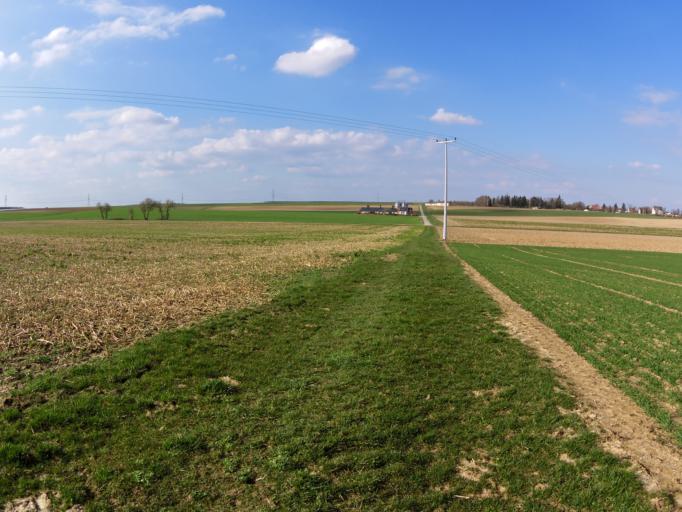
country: DE
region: Bavaria
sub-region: Regierungsbezirk Unterfranken
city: Biebelried
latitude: 49.7881
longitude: 10.0818
